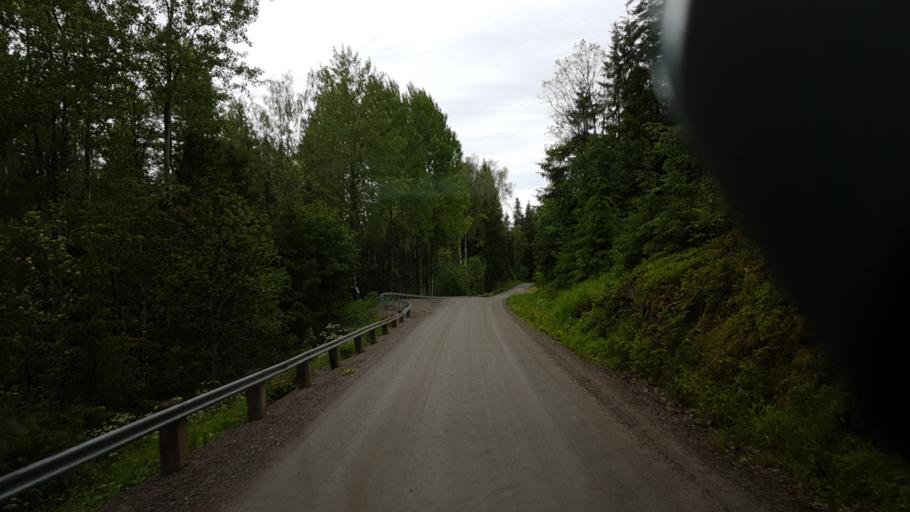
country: NO
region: Ostfold
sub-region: Romskog
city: Romskog
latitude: 59.7098
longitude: 11.9687
